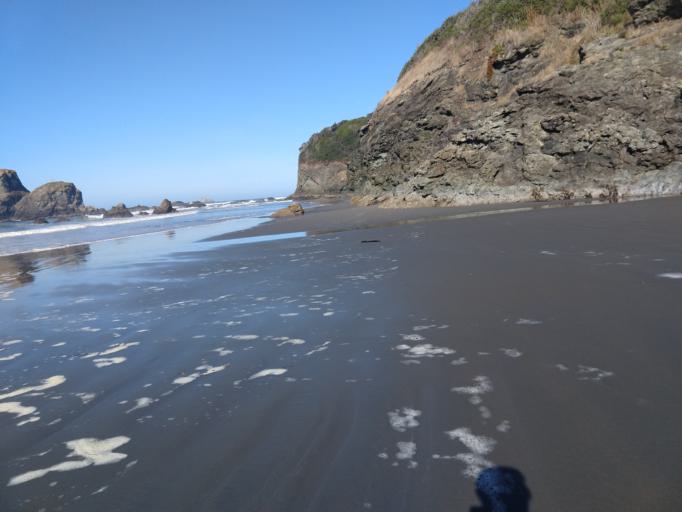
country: US
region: California
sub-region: Humboldt County
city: Westhaven-Moonstone
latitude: 41.0353
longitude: -124.1182
